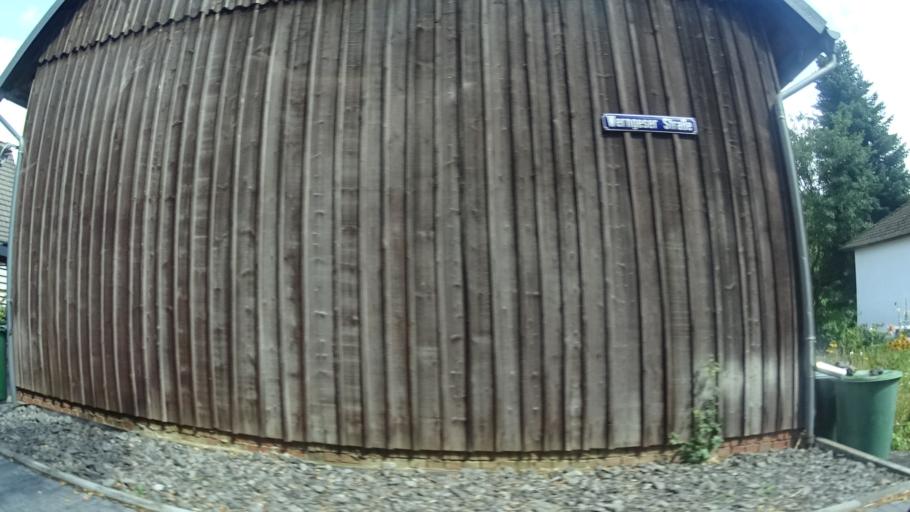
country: DE
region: Hesse
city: Grebenau
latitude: 50.7112
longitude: 9.4454
